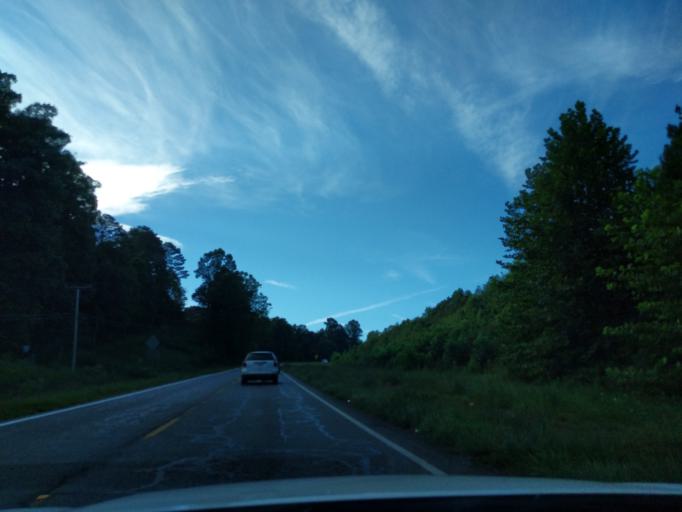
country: US
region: Georgia
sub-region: Fannin County
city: Blue Ridge
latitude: 34.8798
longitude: -84.3248
